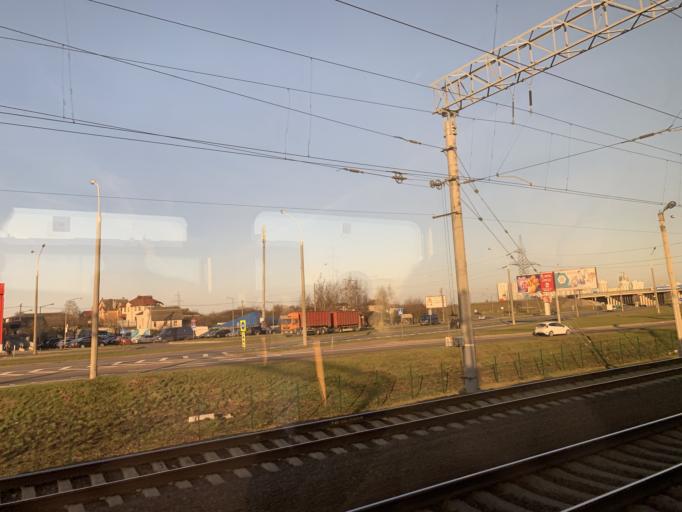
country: BY
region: Minsk
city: Zhdanovichy
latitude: 53.9452
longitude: 27.4316
